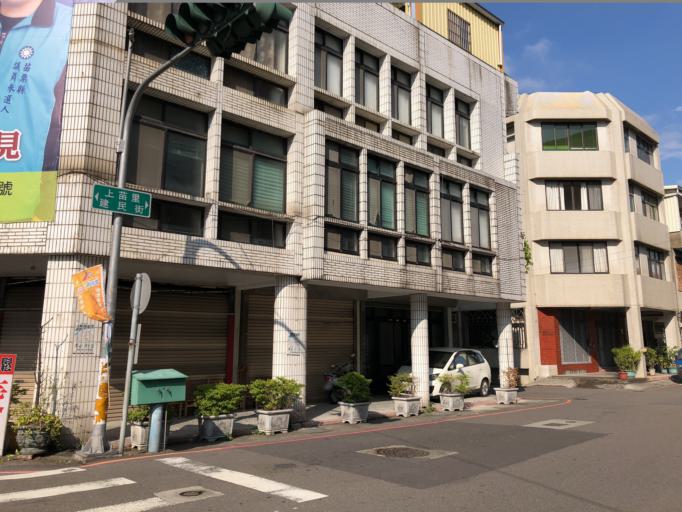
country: TW
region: Taiwan
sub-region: Miaoli
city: Miaoli
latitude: 24.5658
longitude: 120.8242
